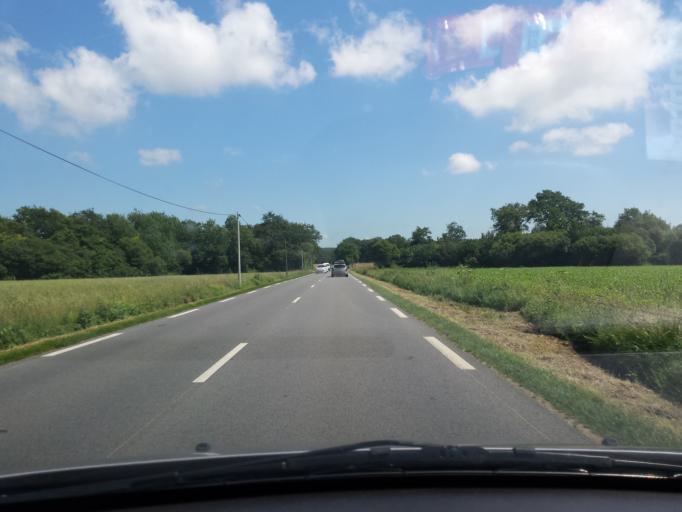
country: FR
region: Pays de la Loire
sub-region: Departement de la Loire-Atlantique
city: Machecoul
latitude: 47.0170
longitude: -1.8642
